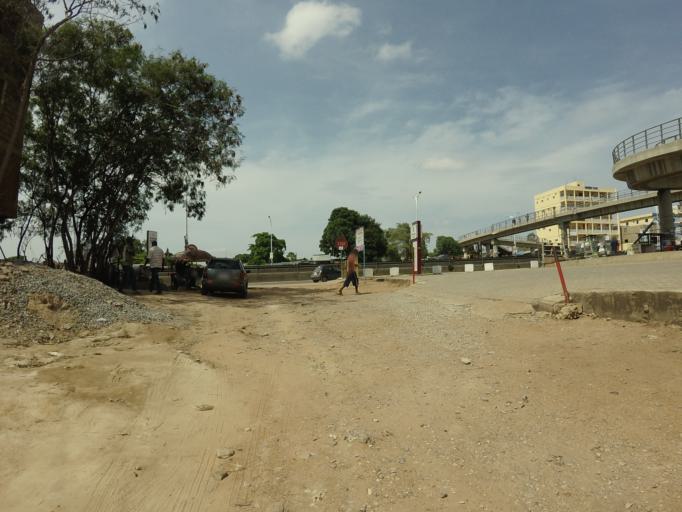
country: GH
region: Greater Accra
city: Dome
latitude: 5.6282
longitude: -0.2353
